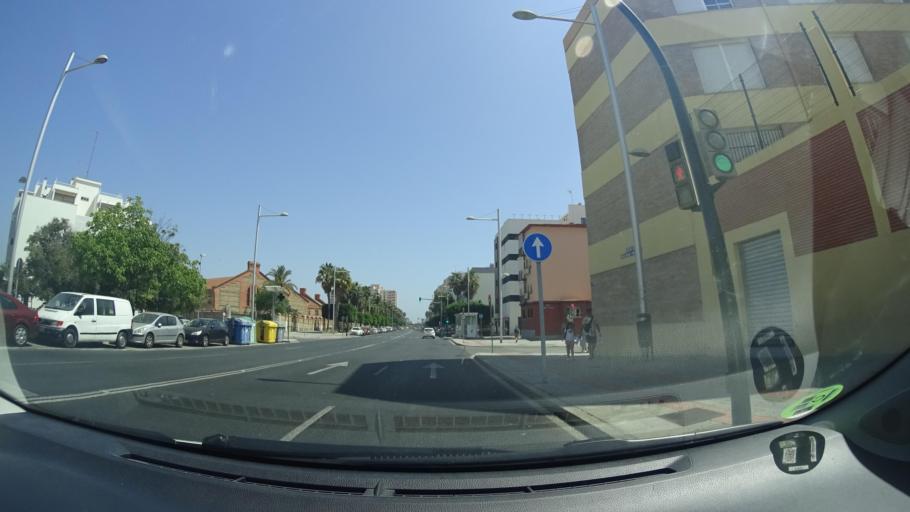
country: ES
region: Andalusia
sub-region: Provincia de Cadiz
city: Cadiz
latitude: 36.5084
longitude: -6.2746
